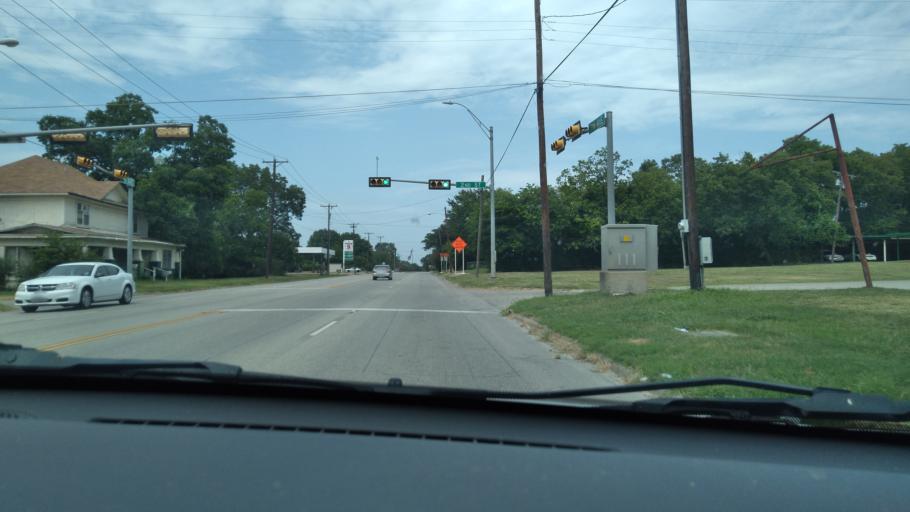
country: US
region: Texas
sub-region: Navarro County
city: Corsicana
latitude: 32.0958
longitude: -96.4548
